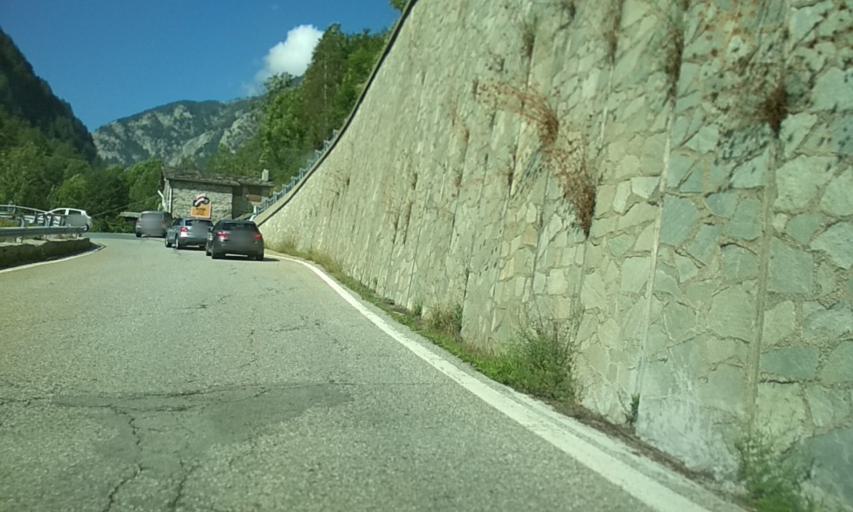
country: IT
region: Piedmont
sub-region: Provincia di Torino
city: Noasca
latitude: 45.4545
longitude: 7.3114
